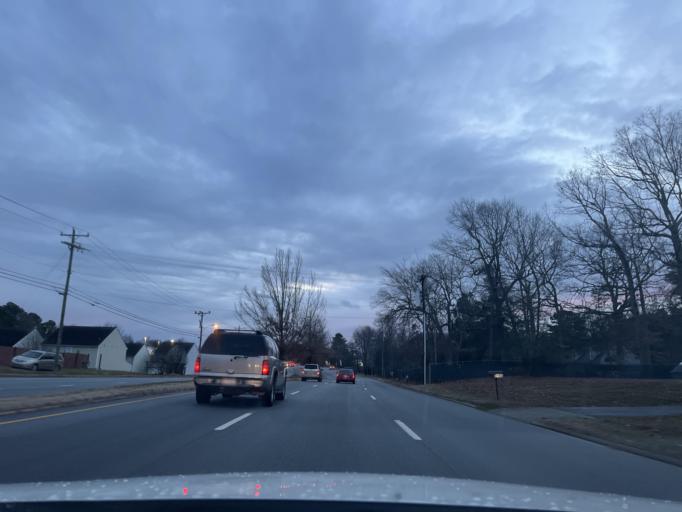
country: US
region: North Carolina
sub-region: Guilford County
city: Greensboro
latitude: 36.0239
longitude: -79.8468
